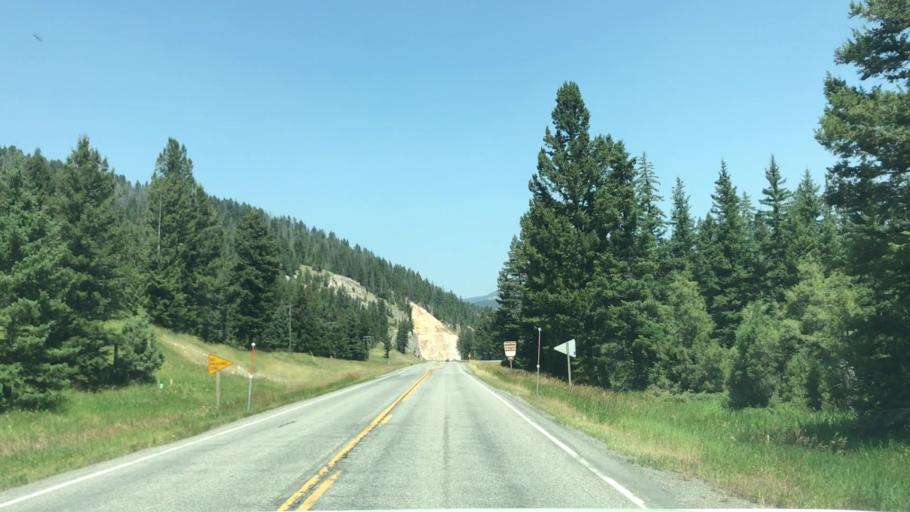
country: US
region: Montana
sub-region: Gallatin County
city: Big Sky
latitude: 45.1719
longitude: -111.2435
